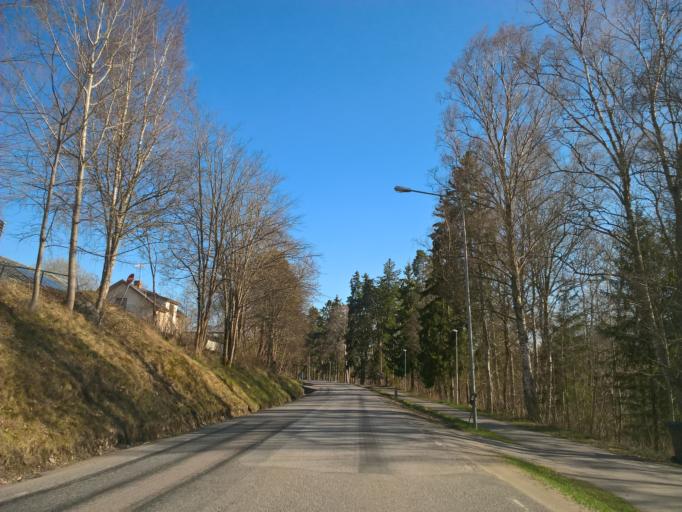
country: SE
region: OEstergoetland
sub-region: Finspangs Kommun
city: Finspang
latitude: 58.7316
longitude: 15.8270
